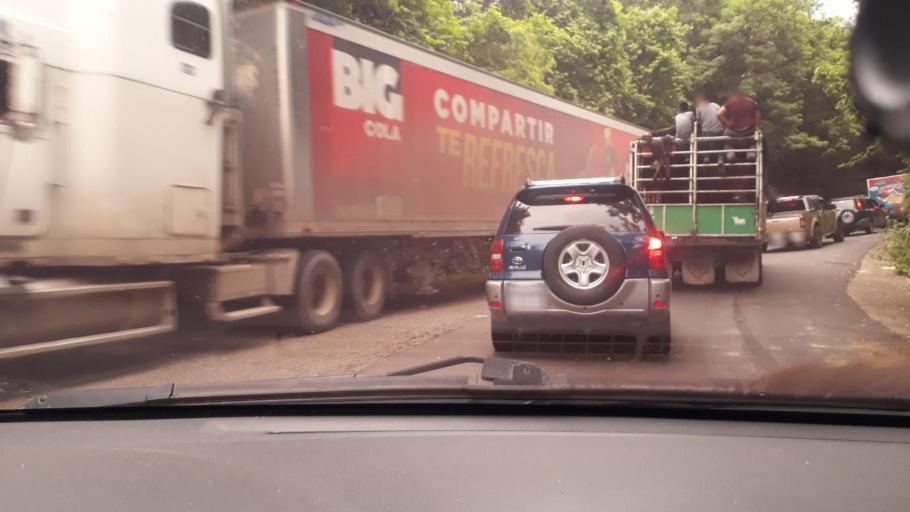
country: GT
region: Jutiapa
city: Jalpatagua
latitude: 14.1676
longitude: -90.0522
